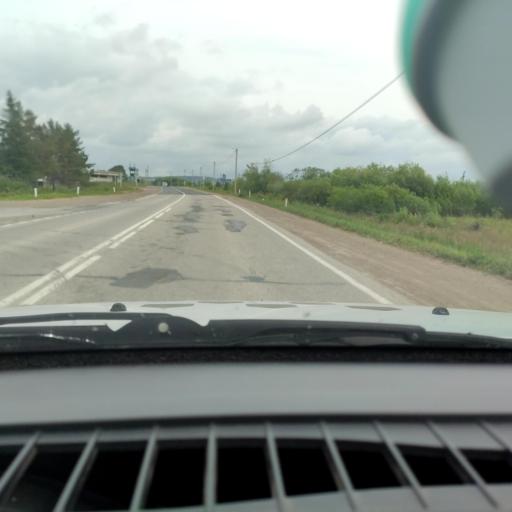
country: RU
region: Perm
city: Ust'-Kishert'
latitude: 57.5934
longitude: 57.3212
